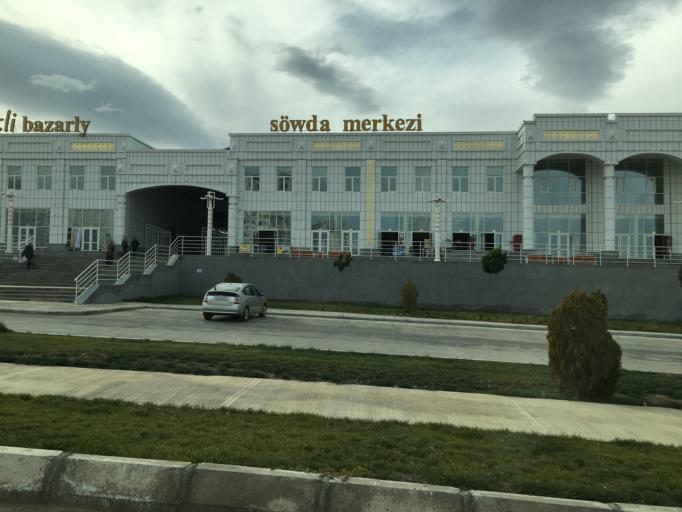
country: TM
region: Ahal
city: Ashgabat
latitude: 37.9015
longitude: 58.4151
